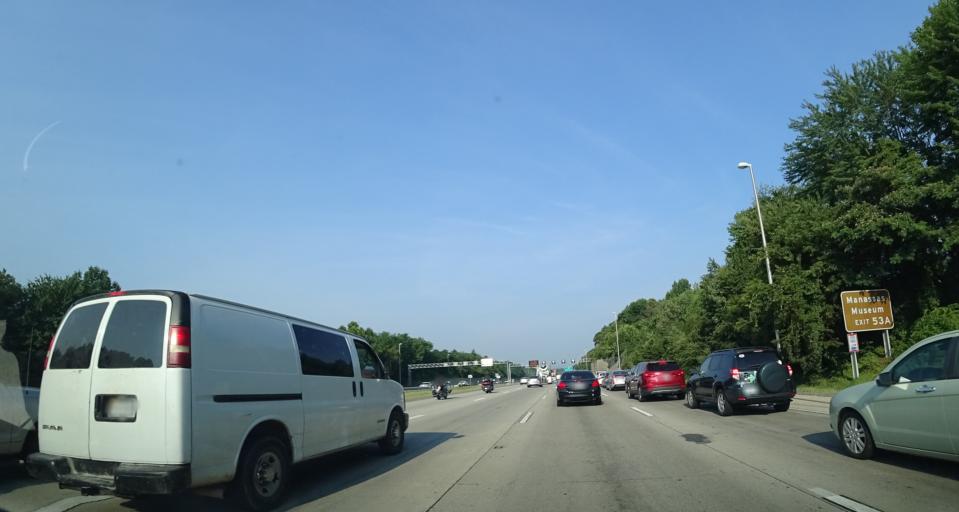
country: US
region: Virginia
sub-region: Fairfax County
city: Centreville
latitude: 38.8487
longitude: -77.4211
